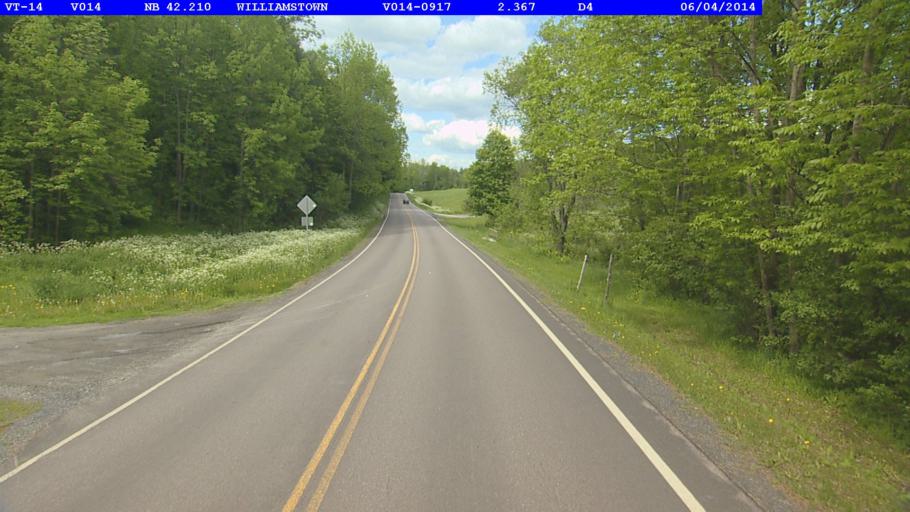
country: US
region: Vermont
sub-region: Orange County
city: Williamstown
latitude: 44.0935
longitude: -72.5500
